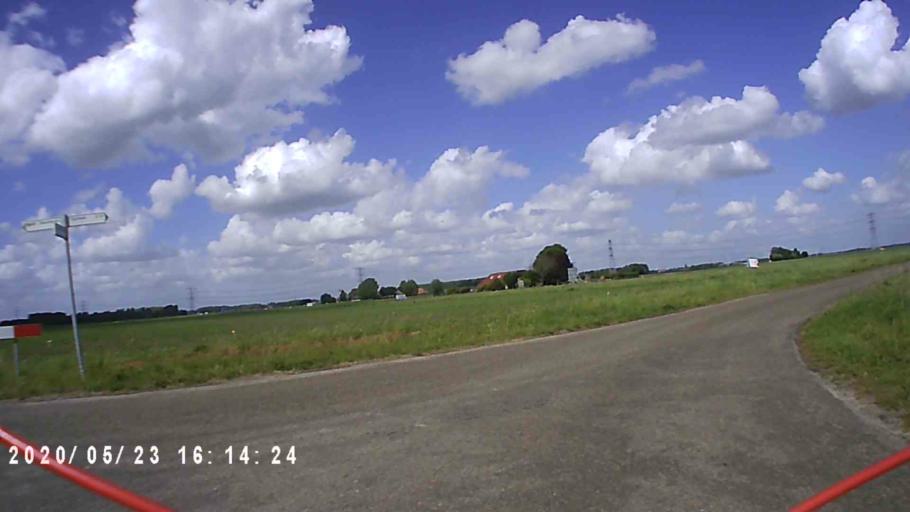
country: NL
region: Groningen
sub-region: Gemeente Appingedam
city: Appingedam
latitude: 53.2545
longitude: 6.8742
